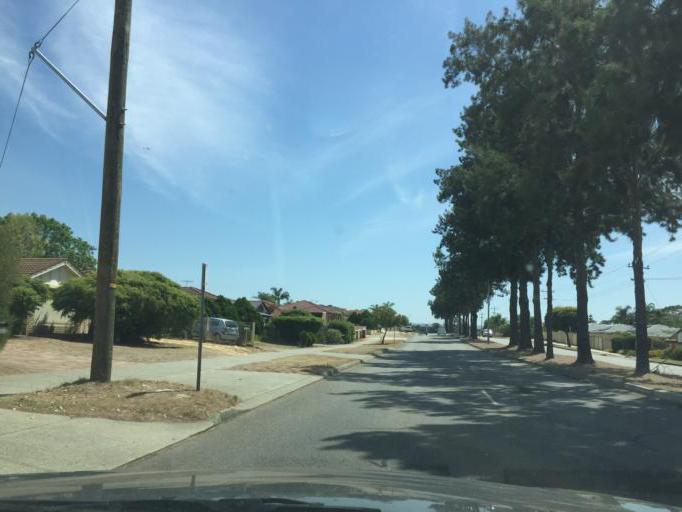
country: AU
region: Western Australia
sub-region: Gosnells
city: Thornlie
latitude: -32.0734
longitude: 115.9633
